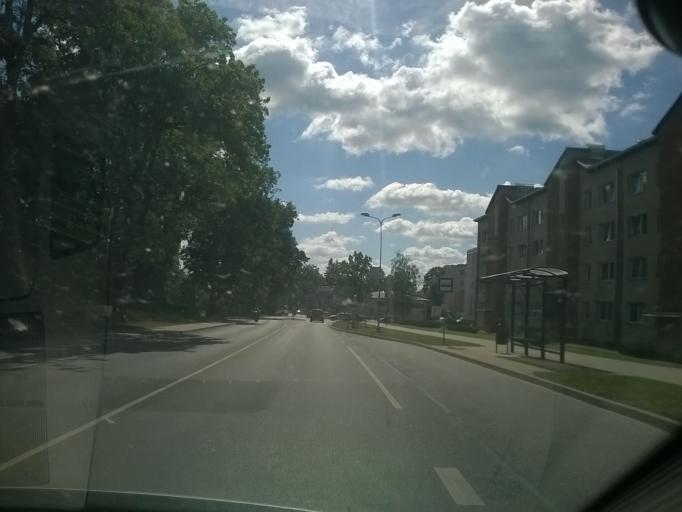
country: LV
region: Aluksnes Rajons
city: Aluksne
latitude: 57.4272
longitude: 27.0401
